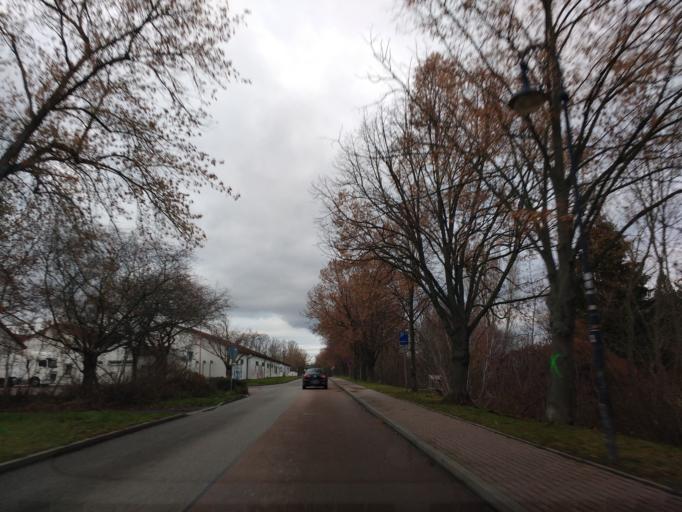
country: DE
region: Saxony-Anhalt
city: Braunsbedra
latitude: 51.2855
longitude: 11.8771
